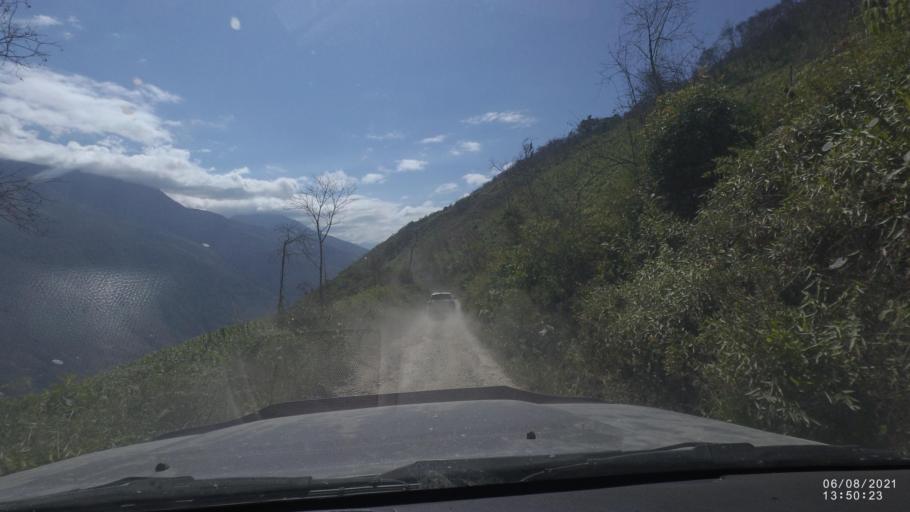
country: BO
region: La Paz
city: Quime
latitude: -16.6570
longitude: -66.7235
